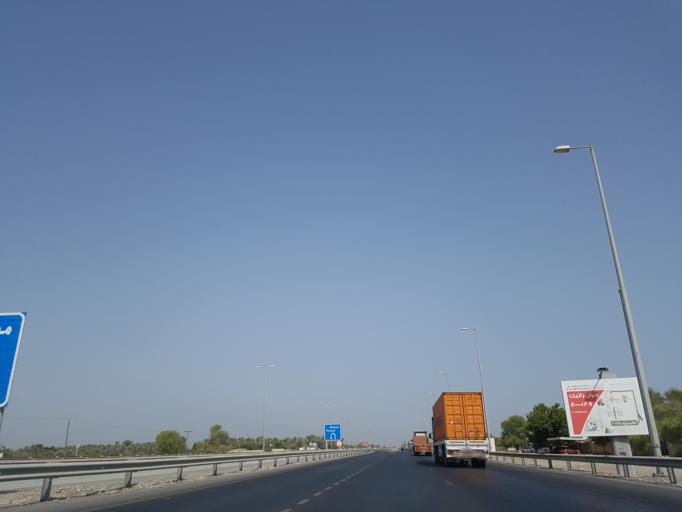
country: OM
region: Al Batinah
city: As Suwayq
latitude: 23.7612
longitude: 57.5551
